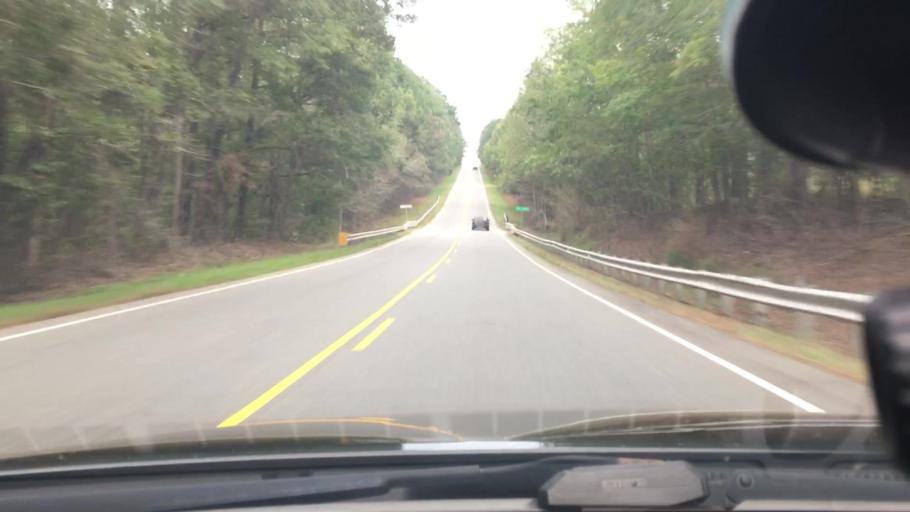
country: US
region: North Carolina
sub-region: Montgomery County
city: Biscoe
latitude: 35.3616
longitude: -79.6934
